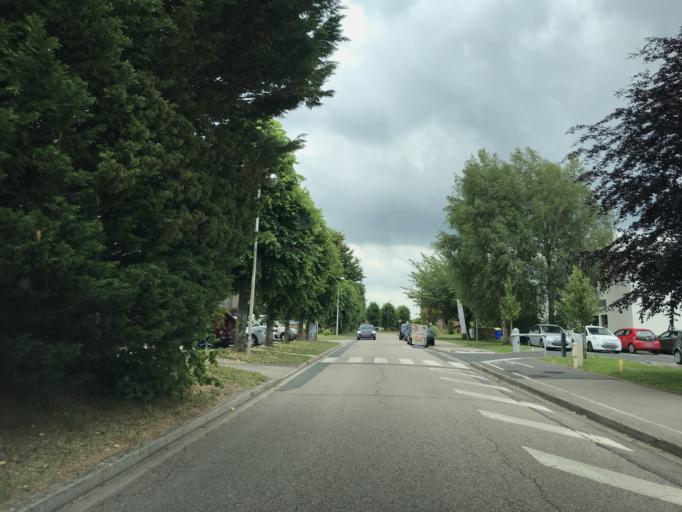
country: FR
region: Haute-Normandie
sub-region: Departement de la Seine-Maritime
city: Mont-Saint-Aignan
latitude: 49.4769
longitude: 1.0952
